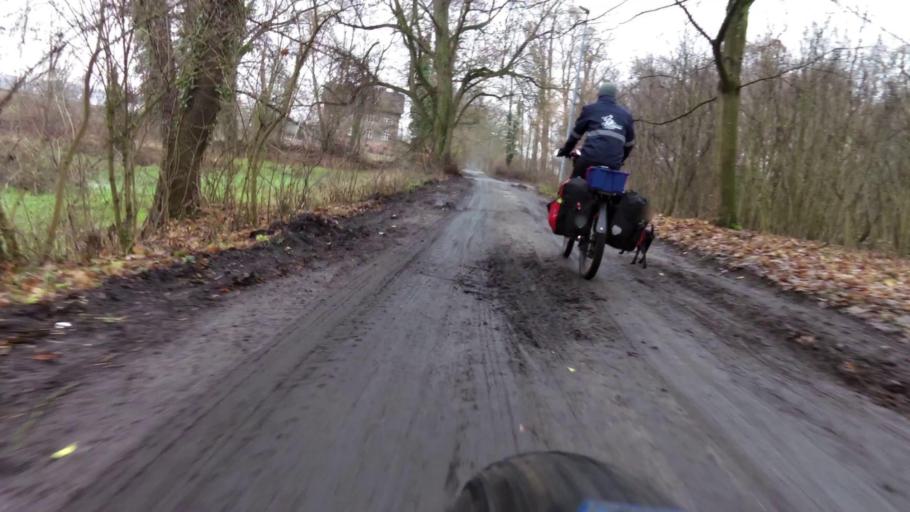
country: PL
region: Lubusz
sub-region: Powiat gorzowski
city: Kostrzyn nad Odra
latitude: 52.6179
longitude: 14.7090
